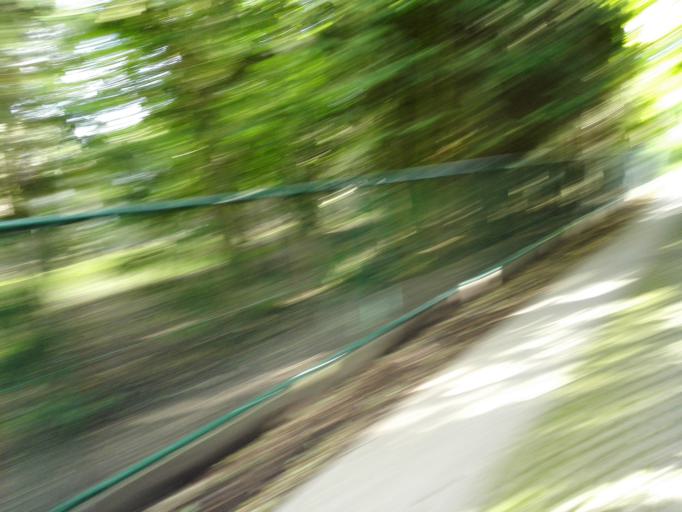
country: BE
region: Flanders
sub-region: Provincie Vlaams-Brabant
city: Keerbergen
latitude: 51.0117
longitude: 4.6030
